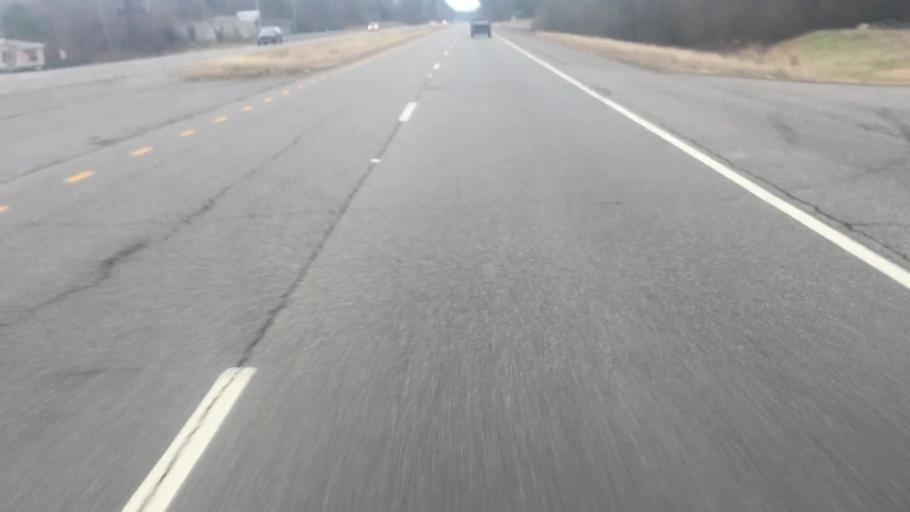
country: US
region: Alabama
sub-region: Walker County
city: Jasper
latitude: 33.8301
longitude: -87.2089
